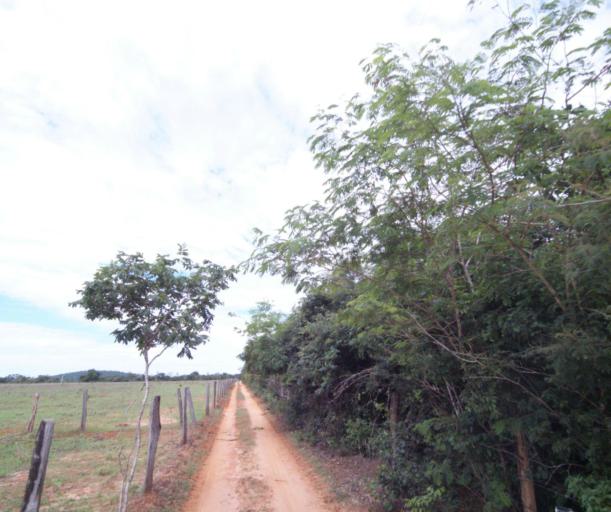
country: BR
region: Bahia
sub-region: Carinhanha
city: Carinhanha
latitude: -14.2338
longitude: -44.3755
